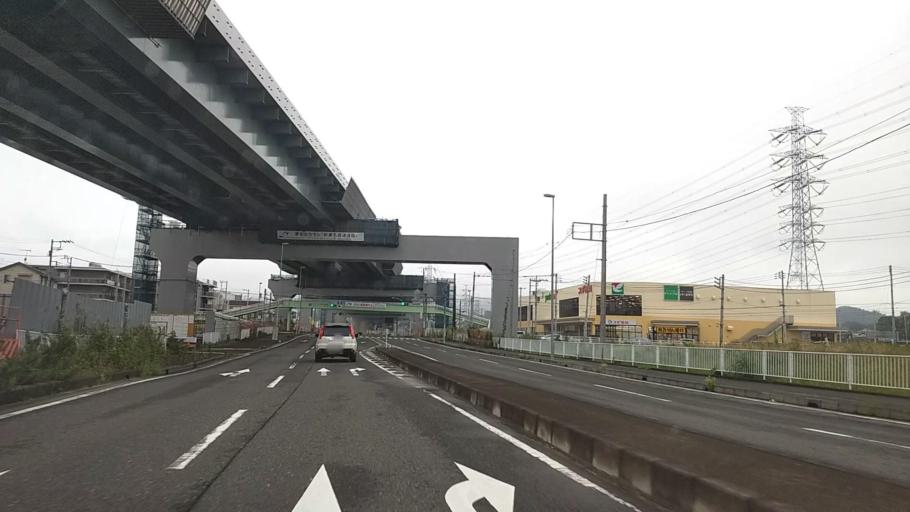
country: JP
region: Kanagawa
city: Isehara
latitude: 35.4074
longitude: 139.3268
